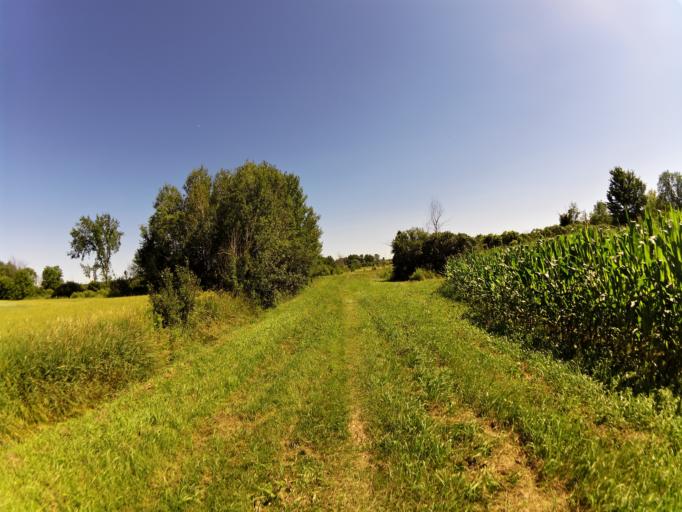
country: CA
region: Ontario
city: Ottawa
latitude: 45.4140
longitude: -75.5896
